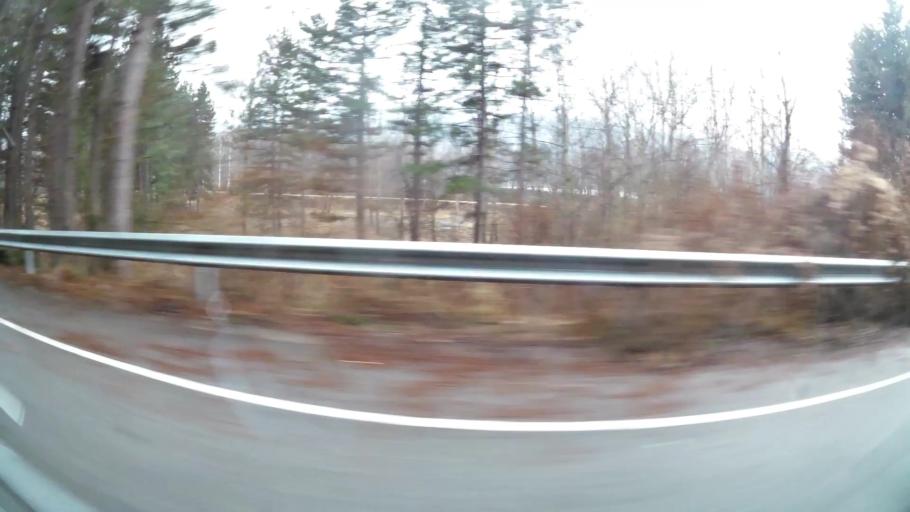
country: BG
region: Sofia-Capital
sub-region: Stolichna Obshtina
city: Sofia
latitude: 42.5871
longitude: 23.4268
